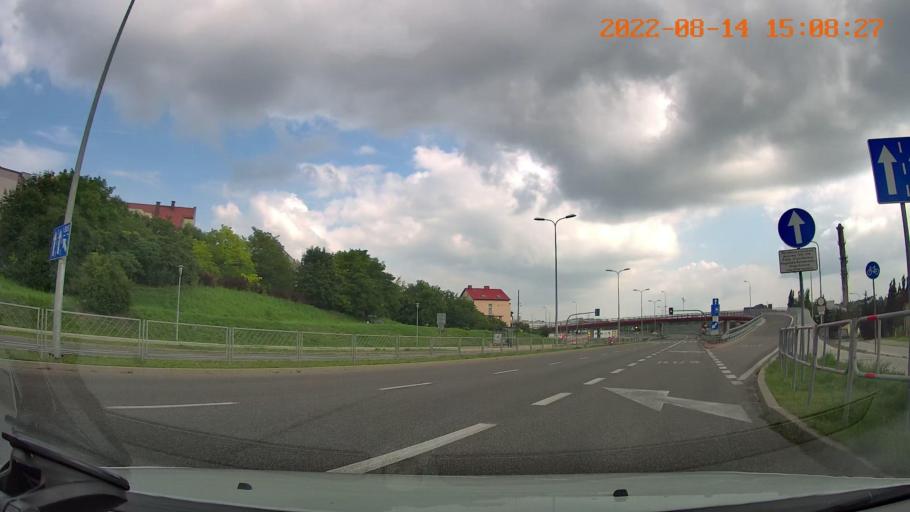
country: PL
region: Swietokrzyskie
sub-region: Powiat kielecki
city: Kielce
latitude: 50.8782
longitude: 20.5916
